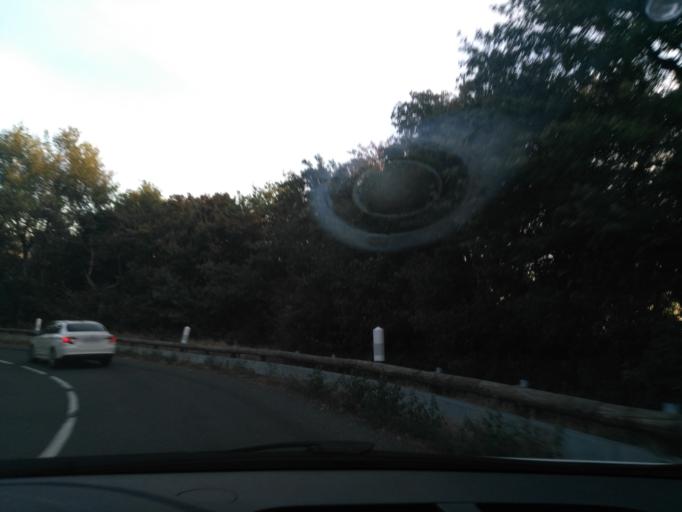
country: FR
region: Rhone-Alpes
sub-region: Departement du Rhone
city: Limonest
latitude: 45.8474
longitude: 4.7961
